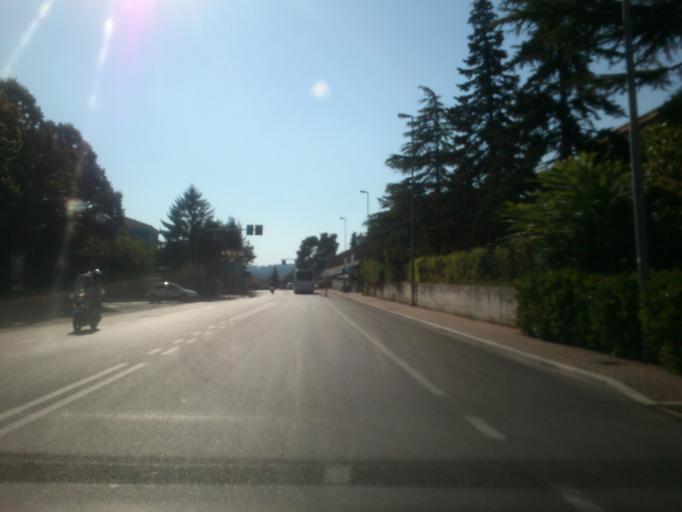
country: IT
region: The Marches
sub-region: Provincia di Pesaro e Urbino
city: Pesaro
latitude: 43.9106
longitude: 12.8903
